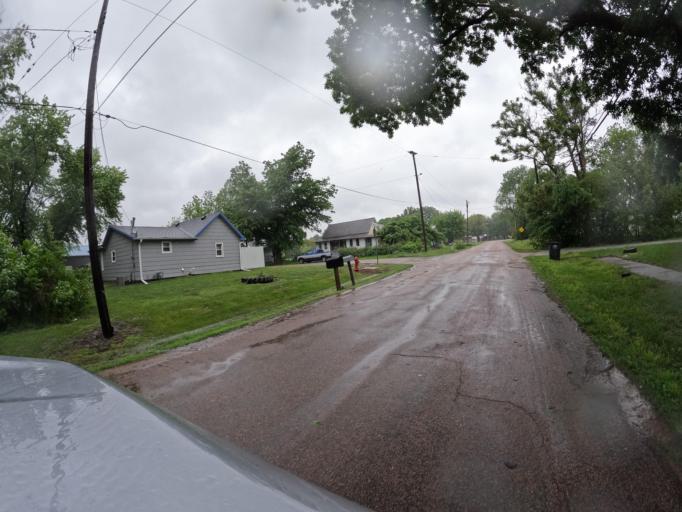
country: US
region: Nebraska
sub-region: Gage County
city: Wymore
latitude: 40.1244
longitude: -96.6737
